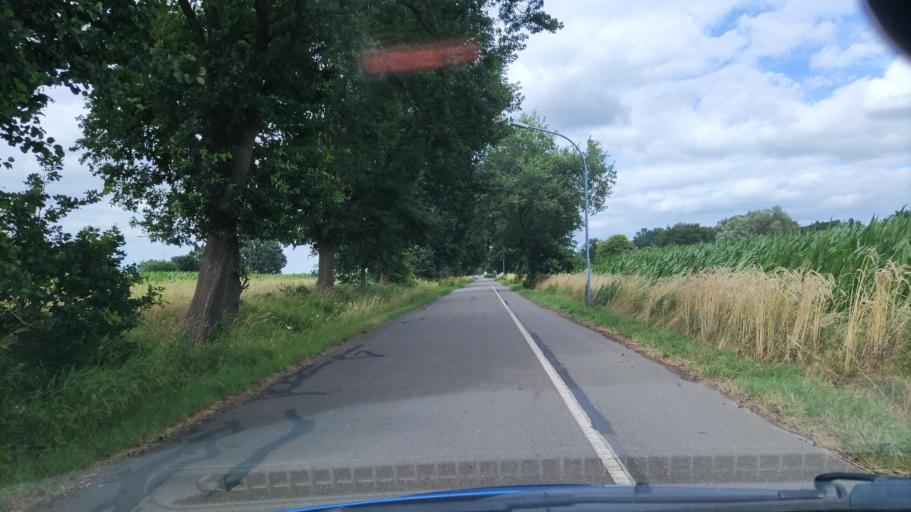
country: DE
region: Lower Saxony
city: Stelle
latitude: 53.4154
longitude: 10.0691
